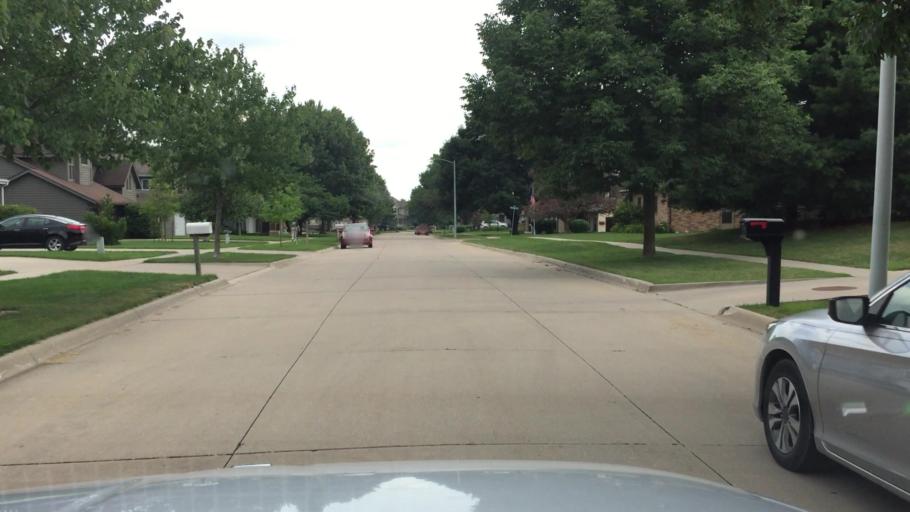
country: US
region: Iowa
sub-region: Johnson County
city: Iowa City
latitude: 41.6654
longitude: -91.4938
